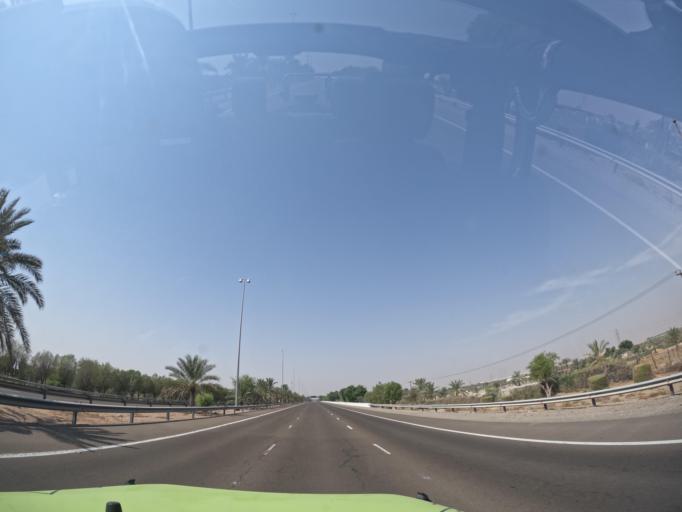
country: AE
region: Abu Dhabi
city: Al Ain
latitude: 24.1986
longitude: 55.3656
